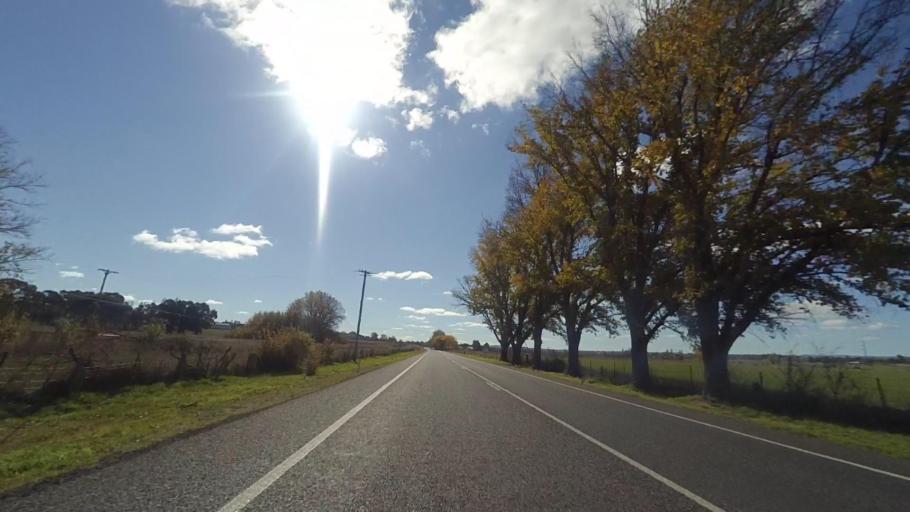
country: AU
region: New South Wales
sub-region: Bathurst Regional
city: Bathurst
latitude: -33.4495
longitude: 149.5789
